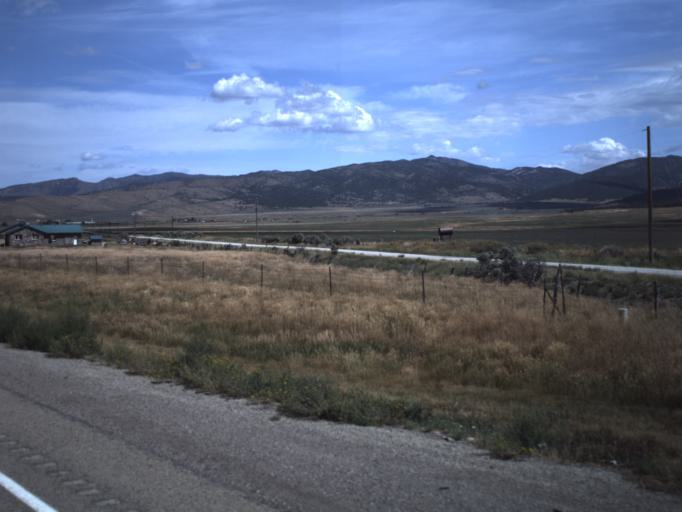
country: US
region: Utah
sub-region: Sanpete County
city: Fairview
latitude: 39.7750
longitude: -111.4894
